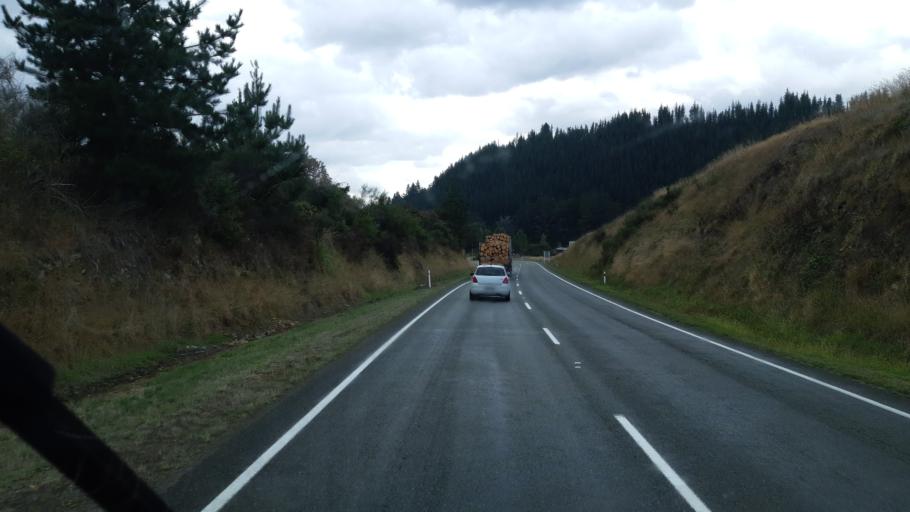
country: NZ
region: Tasman
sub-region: Tasman District
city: Wakefield
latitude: -41.4634
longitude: 172.9485
